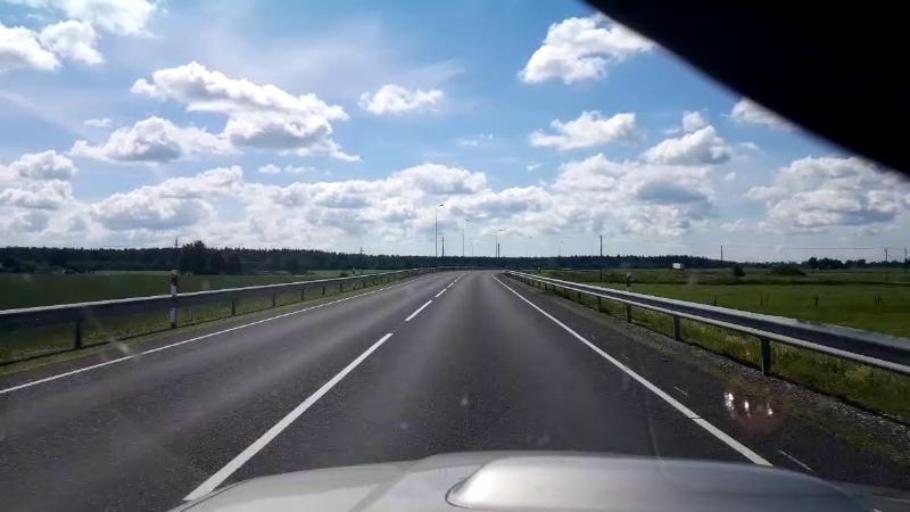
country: EE
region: Jaervamaa
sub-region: Jaerva-Jaani vald
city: Jarva-Jaani
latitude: 59.1439
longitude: 25.7710
